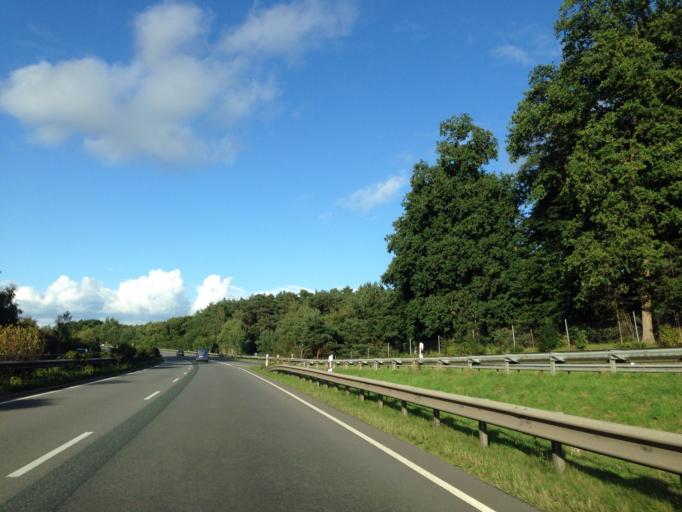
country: DE
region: Lower Saxony
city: Deutsch Evern
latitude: 53.2139
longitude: 10.4427
